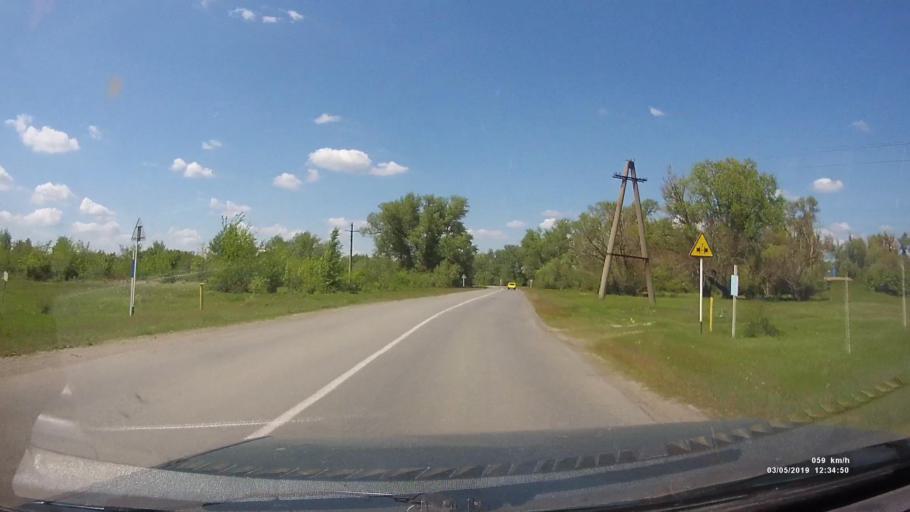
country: RU
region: Rostov
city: Semikarakorsk
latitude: 47.5232
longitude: 40.7654
